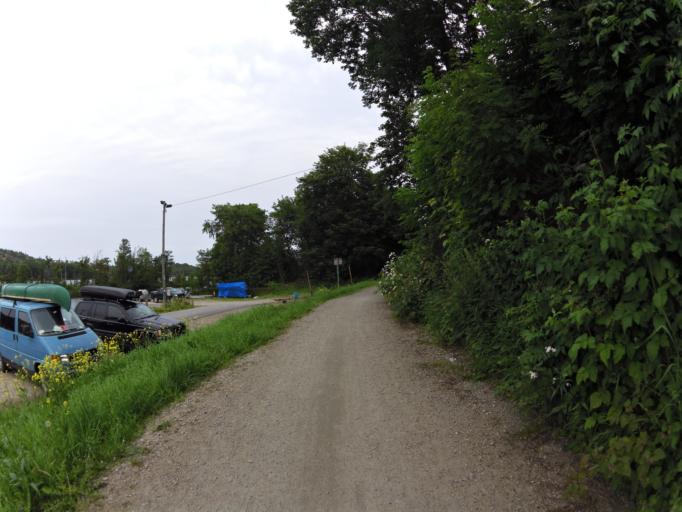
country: NO
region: Ostfold
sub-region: Fredrikstad
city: Fredrikstad
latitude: 59.2177
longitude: 10.9712
